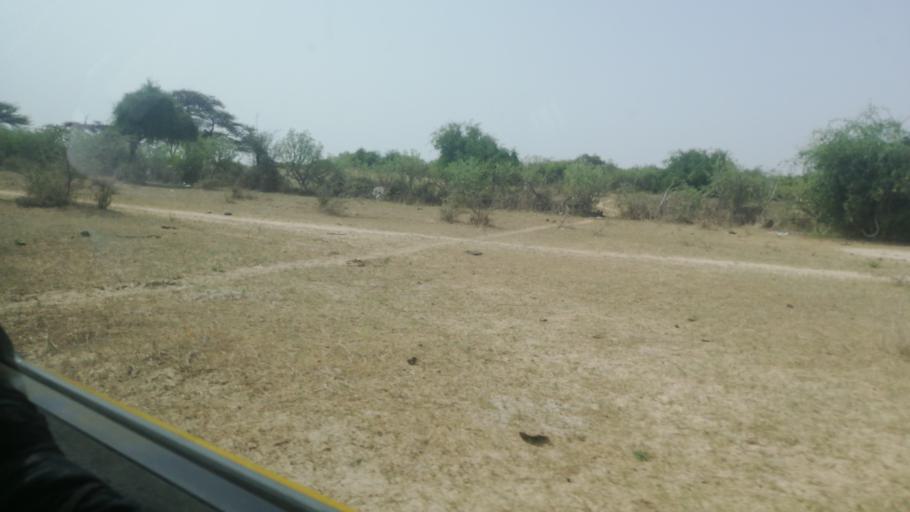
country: SN
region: Saint-Louis
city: Saint-Louis
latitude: 16.0538
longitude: -16.3356
